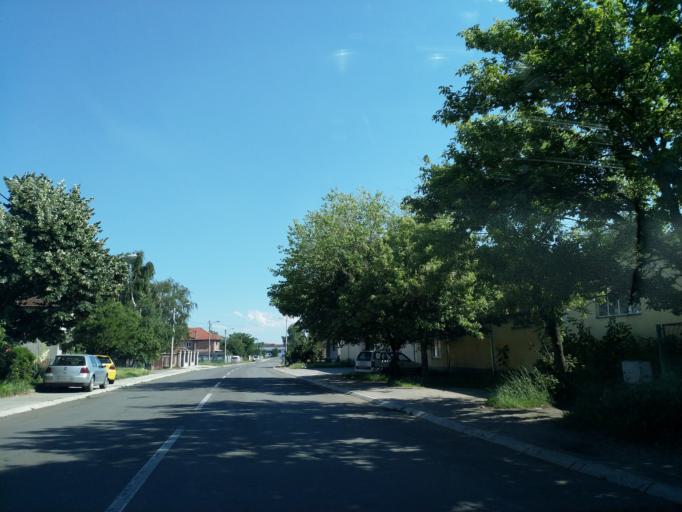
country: RS
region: Central Serbia
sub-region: Pomoravski Okrug
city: Paracin
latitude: 43.8498
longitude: 21.4114
